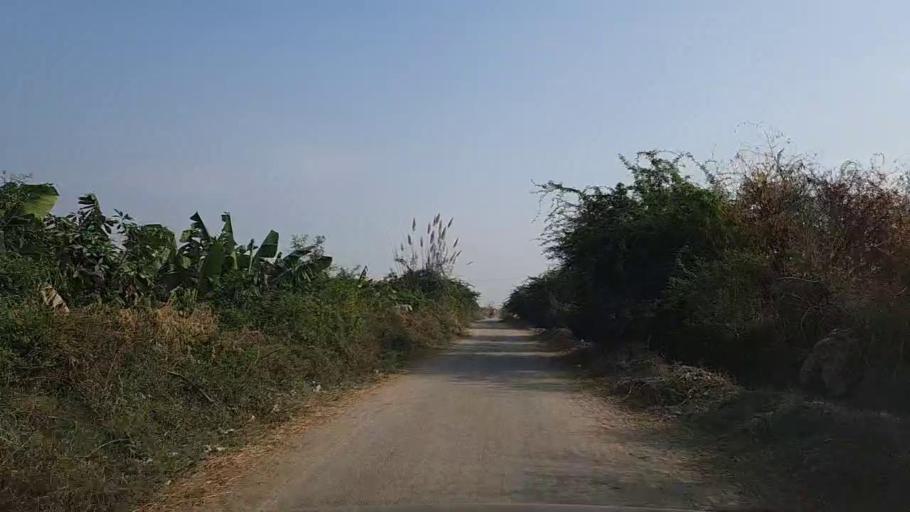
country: PK
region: Sindh
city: Thatta
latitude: 24.6510
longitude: 67.9237
